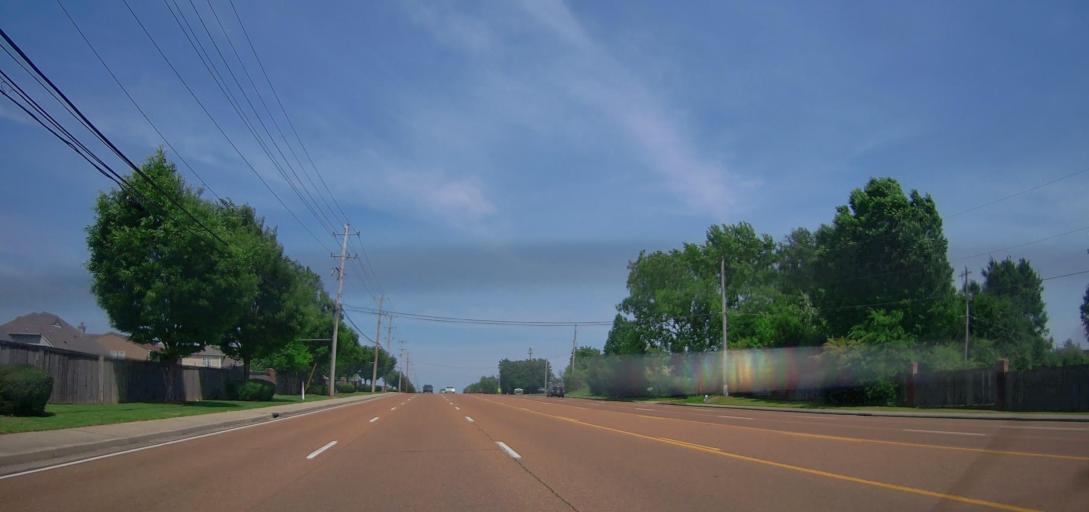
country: US
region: Mississippi
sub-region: De Soto County
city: Olive Branch
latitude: 35.0205
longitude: -89.8070
